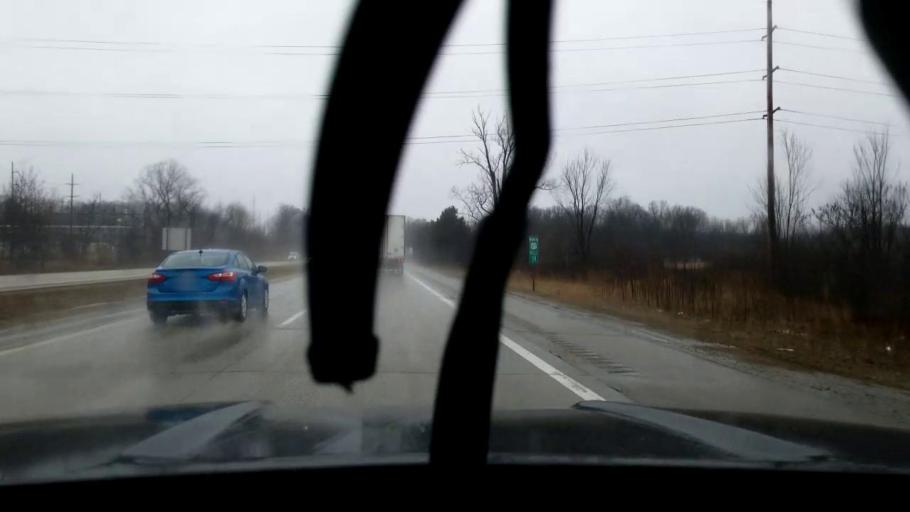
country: US
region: Michigan
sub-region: Jackson County
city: Michigan Center
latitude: 42.2446
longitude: -84.3560
